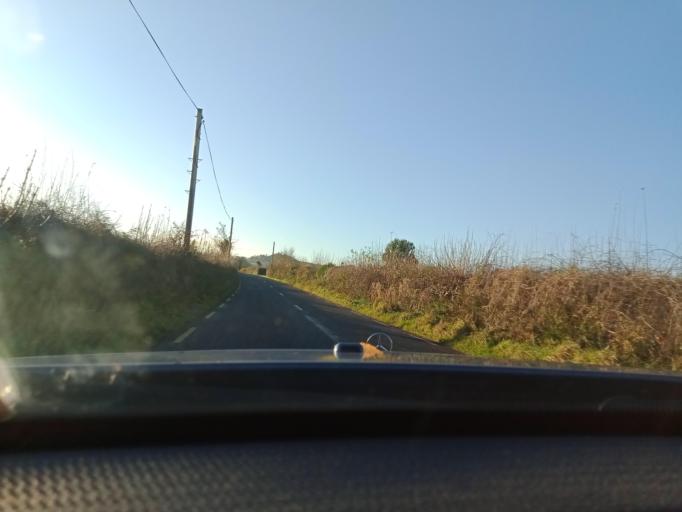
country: IE
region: Leinster
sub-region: Kilkenny
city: Callan
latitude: 52.4768
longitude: -7.3920
